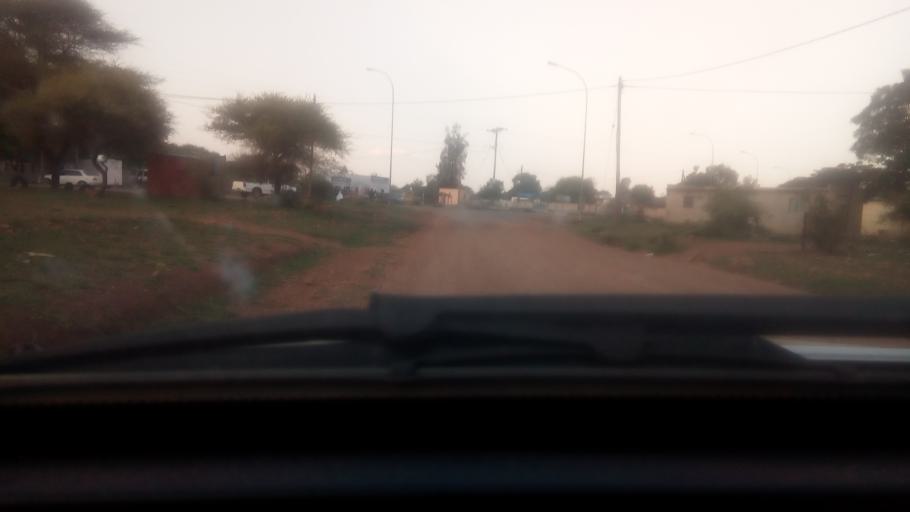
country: BW
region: Kgatleng
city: Bokaa
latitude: -24.4268
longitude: 26.0163
